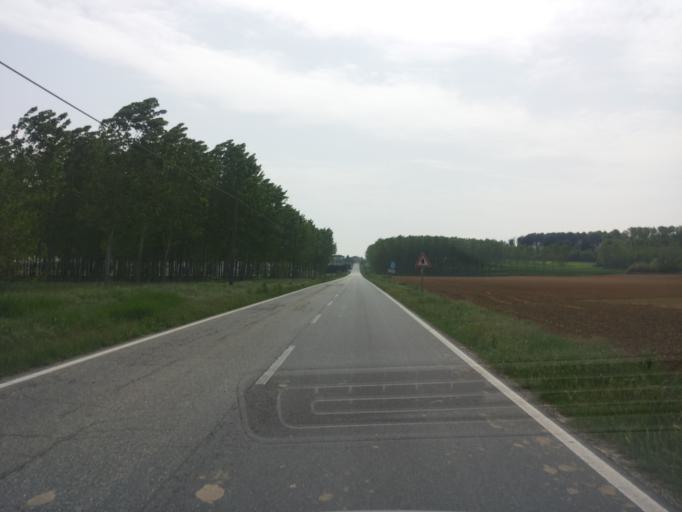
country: IT
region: Piedmont
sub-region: Provincia di Alessandria
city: Mirabello Monferrato
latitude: 45.0458
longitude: 8.5198
